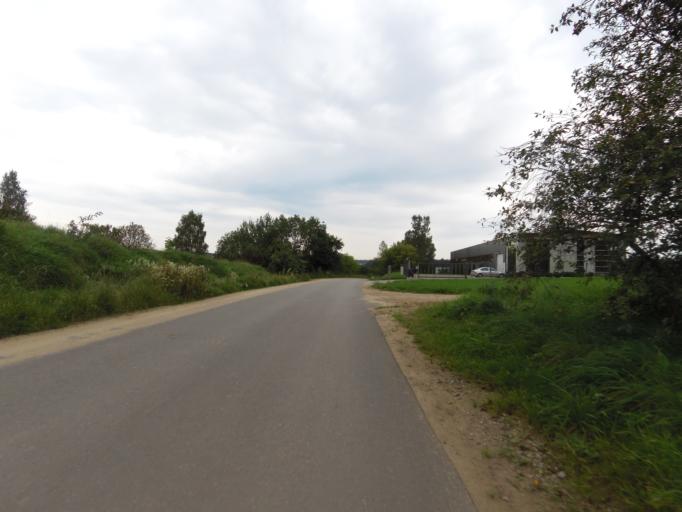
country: LT
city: Grigiskes
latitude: 54.7049
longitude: 25.1252
